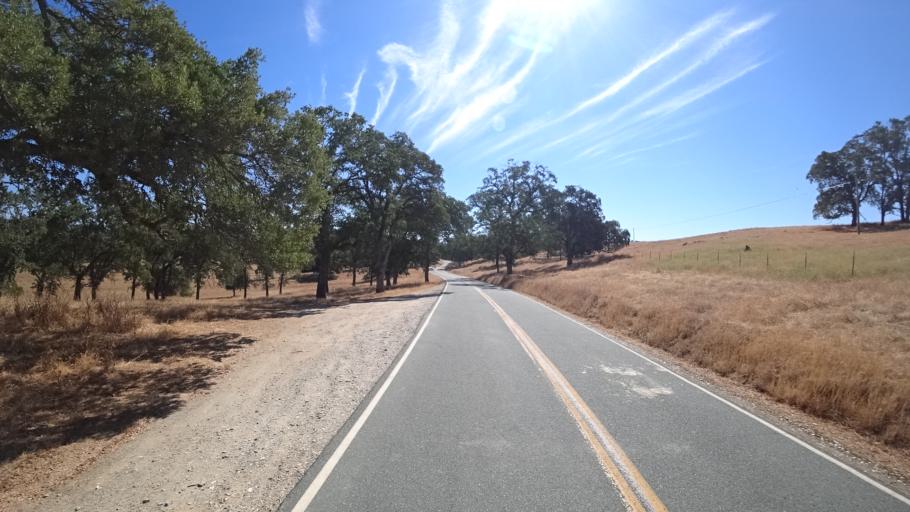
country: US
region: California
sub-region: Calaveras County
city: San Andreas
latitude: 38.1483
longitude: -120.6052
